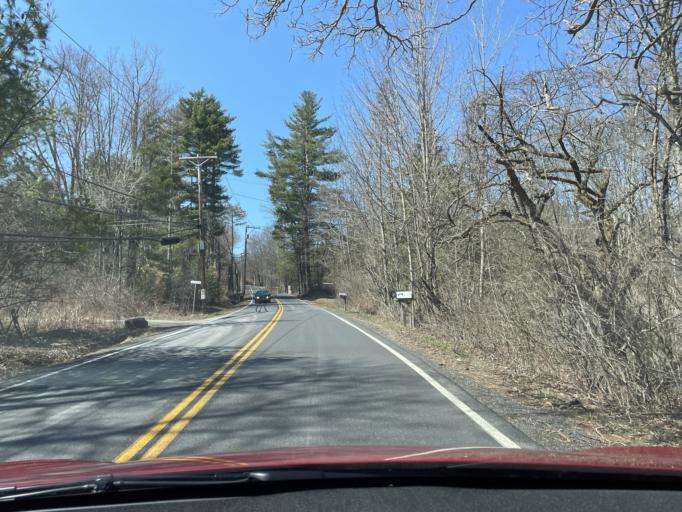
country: US
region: New York
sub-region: Ulster County
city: Woodstock
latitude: 42.0382
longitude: -74.1646
